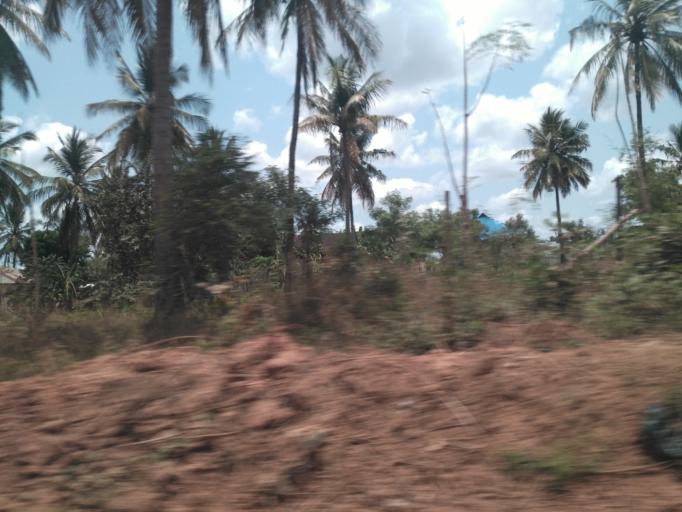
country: TZ
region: Dar es Salaam
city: Dar es Salaam
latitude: -6.8408
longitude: 39.3362
